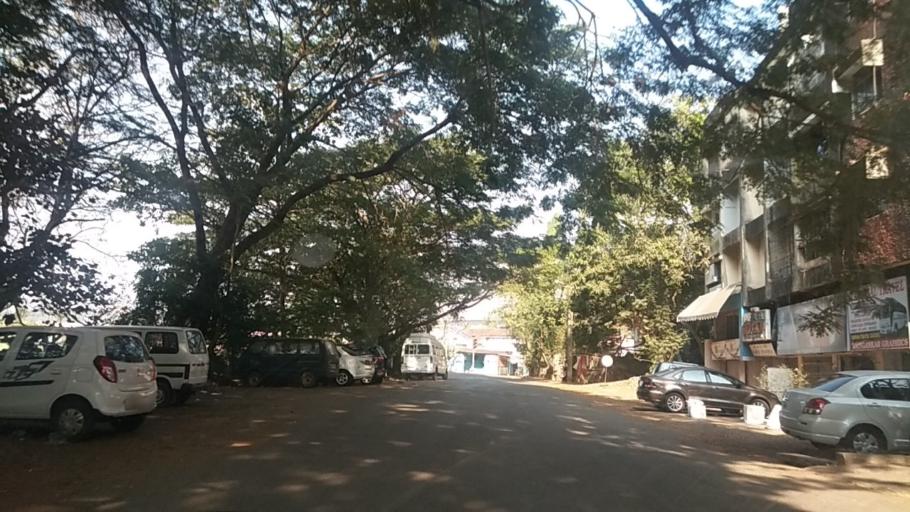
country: IN
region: Goa
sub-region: North Goa
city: Panaji
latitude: 15.4979
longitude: 73.8341
